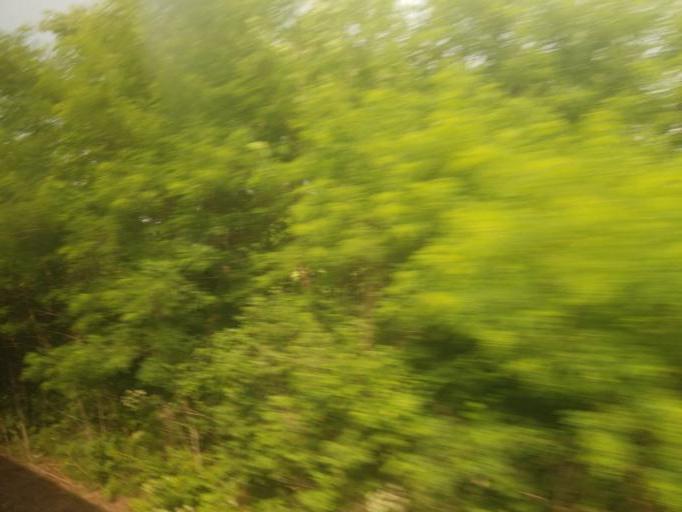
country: US
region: Illinois
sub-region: Bureau County
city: Princeton
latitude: 41.3239
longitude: -89.6799
